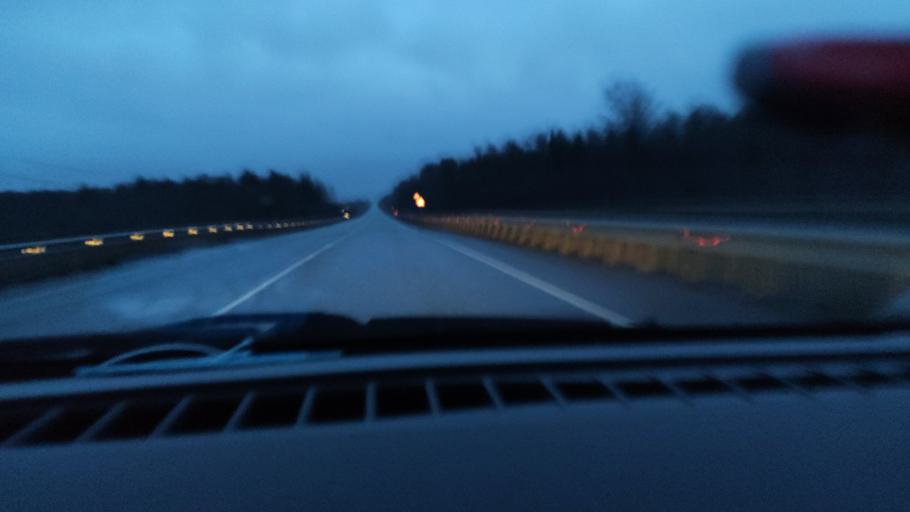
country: RU
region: Udmurtiya
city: Mozhga
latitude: 56.3619
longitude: 52.2586
